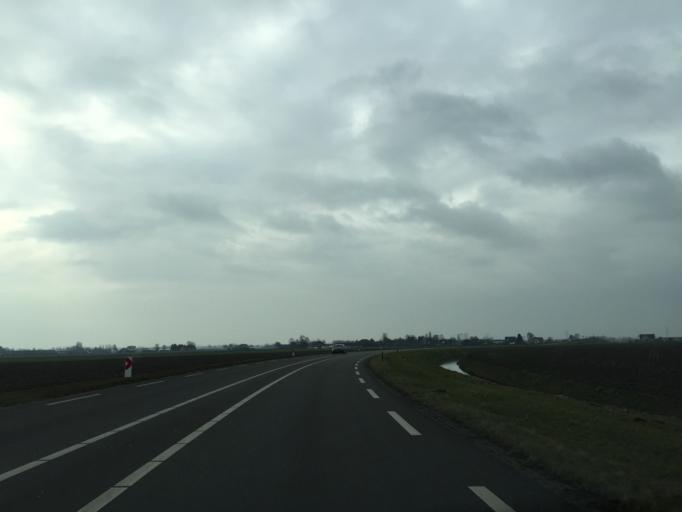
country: NL
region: South Holland
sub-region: Gemeente Waddinxveen
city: Waddinxveen
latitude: 52.0121
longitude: 4.6099
